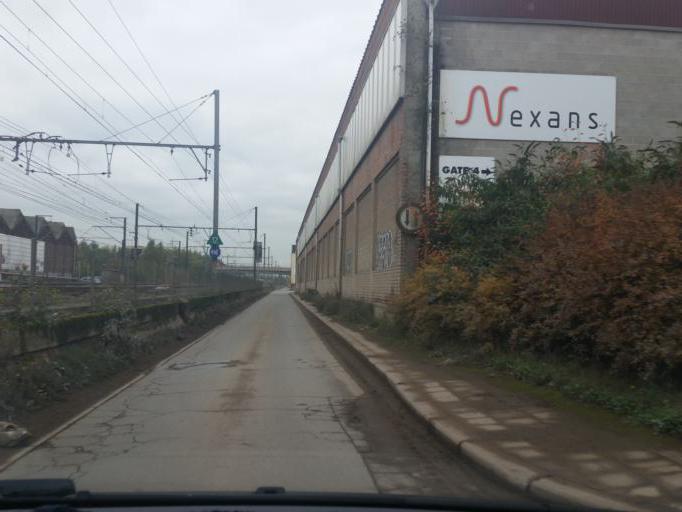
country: BE
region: Flanders
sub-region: Provincie Vlaams-Brabant
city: Sint-Pieters-Leeuw
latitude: 50.7547
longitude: 4.2617
